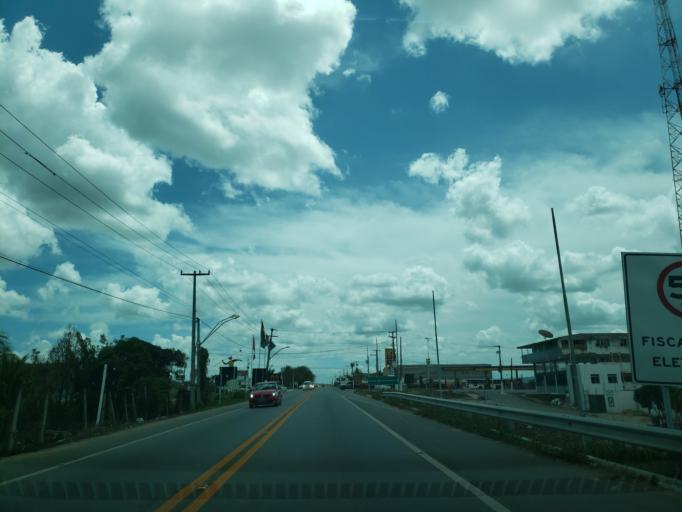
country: BR
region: Alagoas
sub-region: Uniao Dos Palmares
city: Uniao dos Palmares
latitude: -9.1658
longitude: -36.0205
